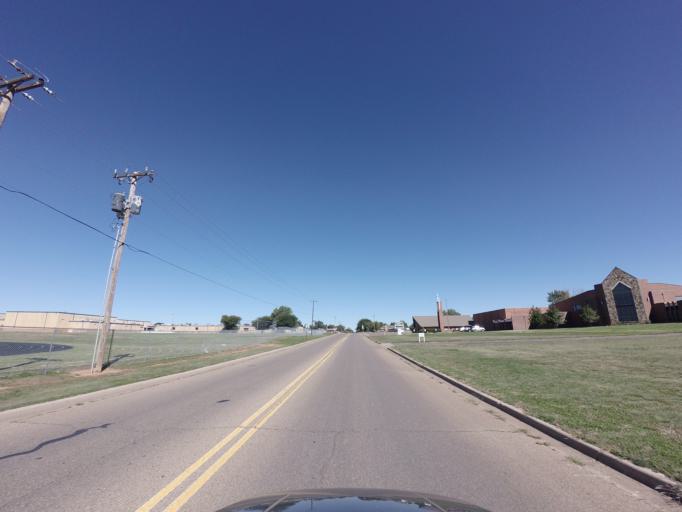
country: US
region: New Mexico
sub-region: Curry County
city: Clovis
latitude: 34.4126
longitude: -103.1877
